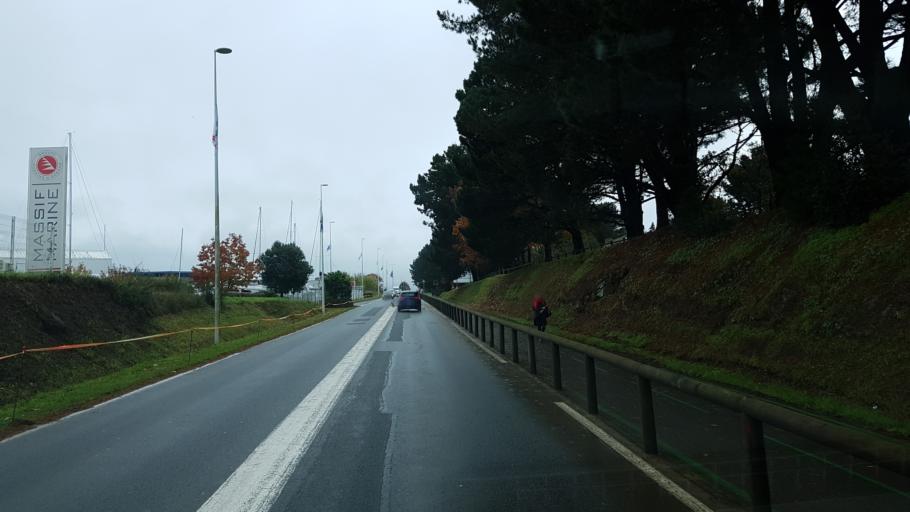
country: FR
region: Brittany
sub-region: Departement du Morbihan
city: Arzon
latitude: 47.5450
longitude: -2.8870
